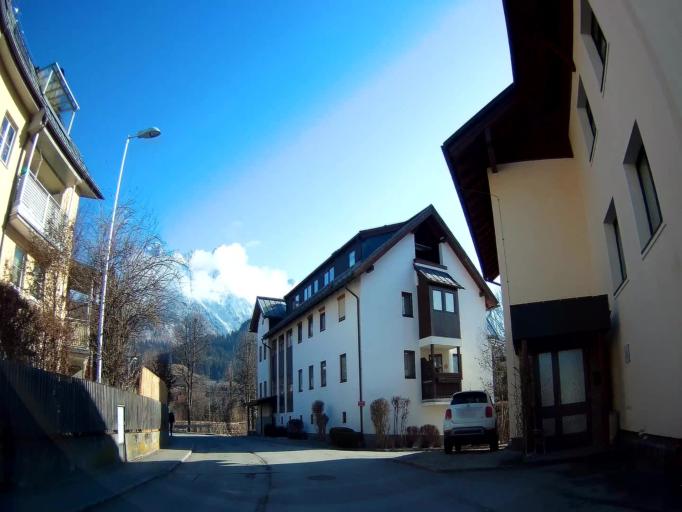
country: AT
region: Salzburg
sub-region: Politischer Bezirk Zell am See
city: Saalfelden am Steinernen Meer
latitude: 47.4279
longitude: 12.8517
